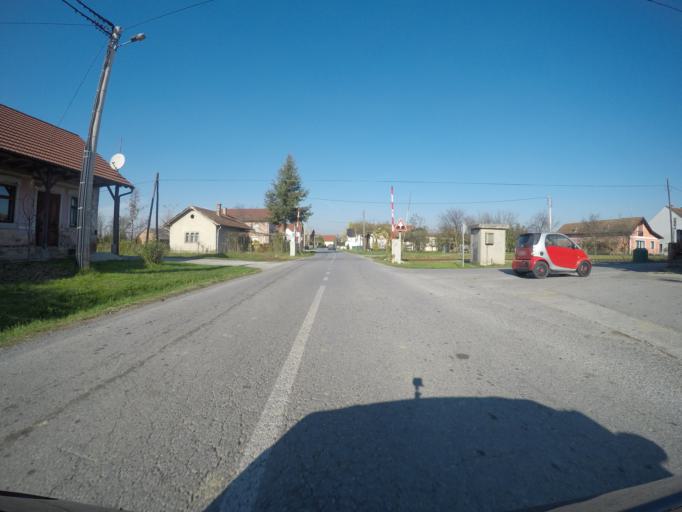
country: HR
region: Bjelovarsko-Bilogorska
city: Predavac
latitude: 45.9103
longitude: 16.7737
